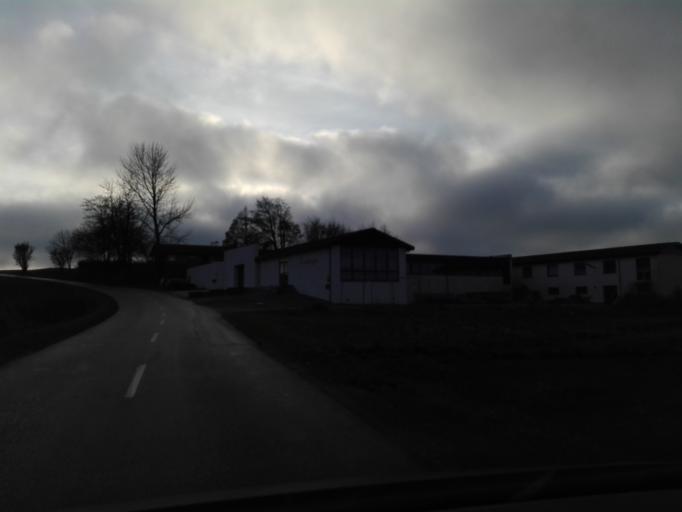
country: DK
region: Central Jutland
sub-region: Arhus Kommune
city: Solbjerg
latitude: 56.0249
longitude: 10.1075
